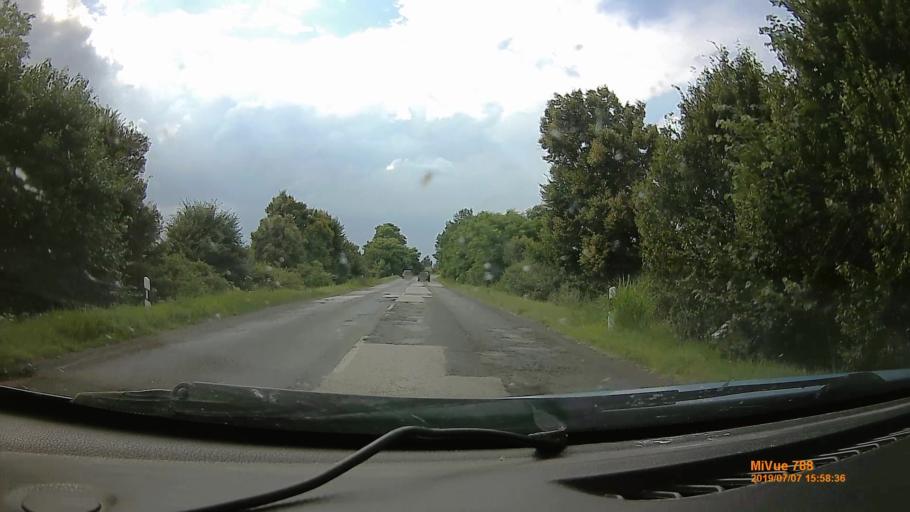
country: HU
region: Pest
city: Szentlorinckata
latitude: 47.5816
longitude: 19.7500
